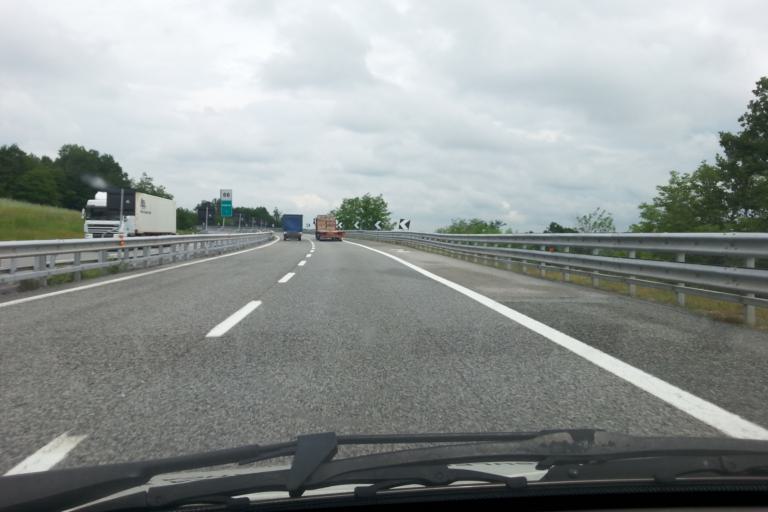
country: IT
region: Piedmont
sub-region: Provincia di Cuneo
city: Bastia Mondovi
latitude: 44.4222
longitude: 7.8881
